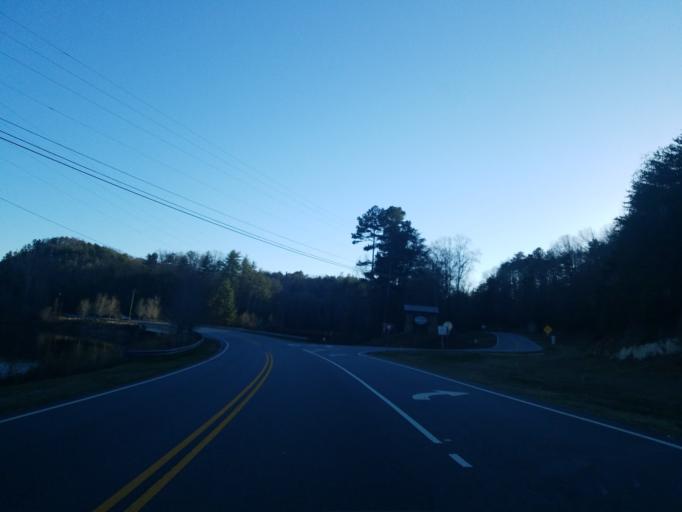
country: US
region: Georgia
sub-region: Lumpkin County
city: Dahlonega
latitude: 34.5488
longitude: -83.9723
